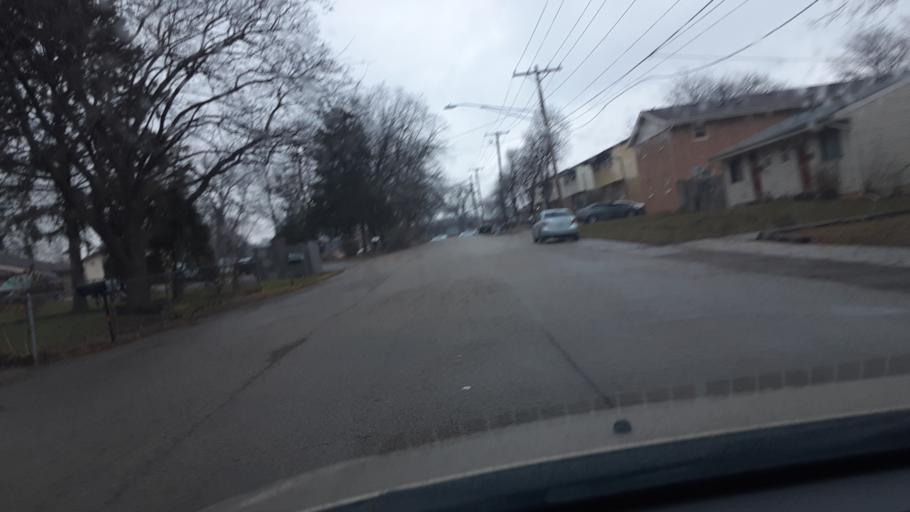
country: US
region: Illinois
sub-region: Winnebago County
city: Rockford
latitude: 42.3086
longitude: -89.1041
